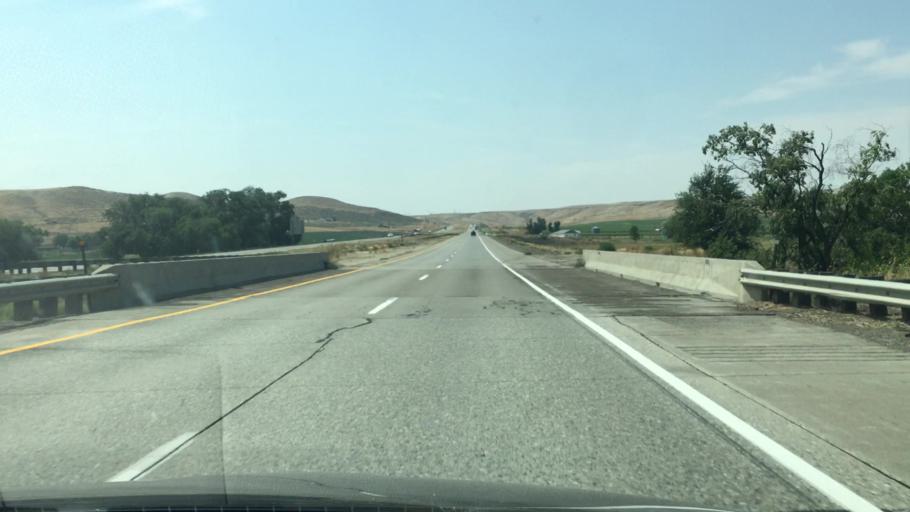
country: US
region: Idaho
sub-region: Elmore County
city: Glenns Ferry
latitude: 42.9608
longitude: -115.3040
